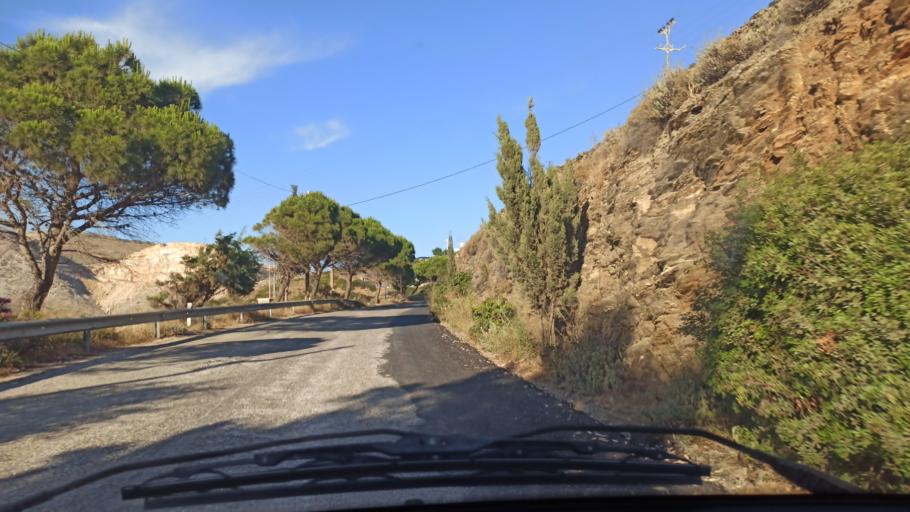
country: GR
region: South Aegean
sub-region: Nomos Kykladon
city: Ano Syros
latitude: 37.4427
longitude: 24.9076
